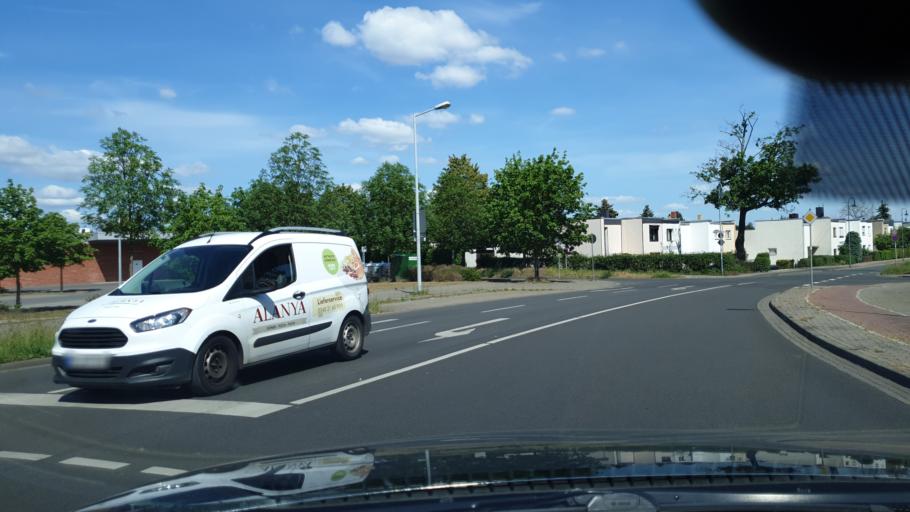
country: DE
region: Saxony-Anhalt
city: Dessau
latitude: 51.8058
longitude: 12.2413
